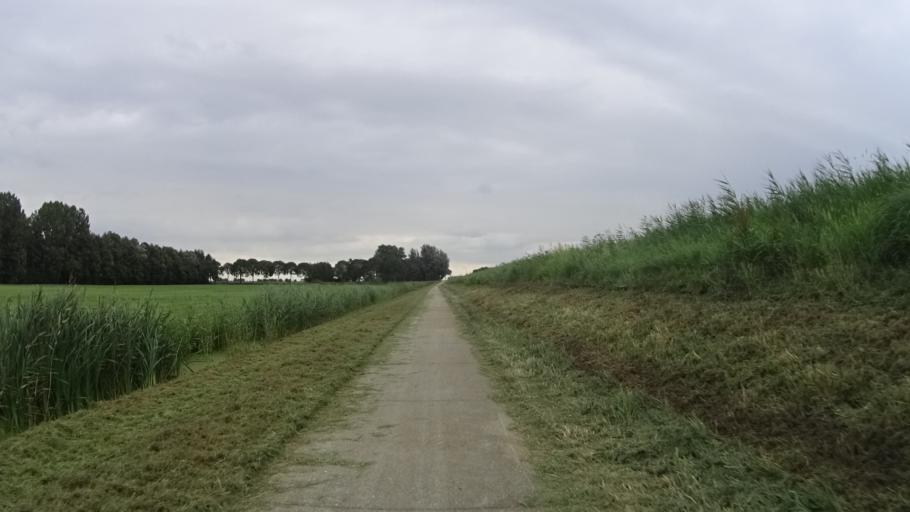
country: NL
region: Groningen
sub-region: Gemeente Groningen
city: Oosterpark
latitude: 53.2357
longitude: 6.6575
